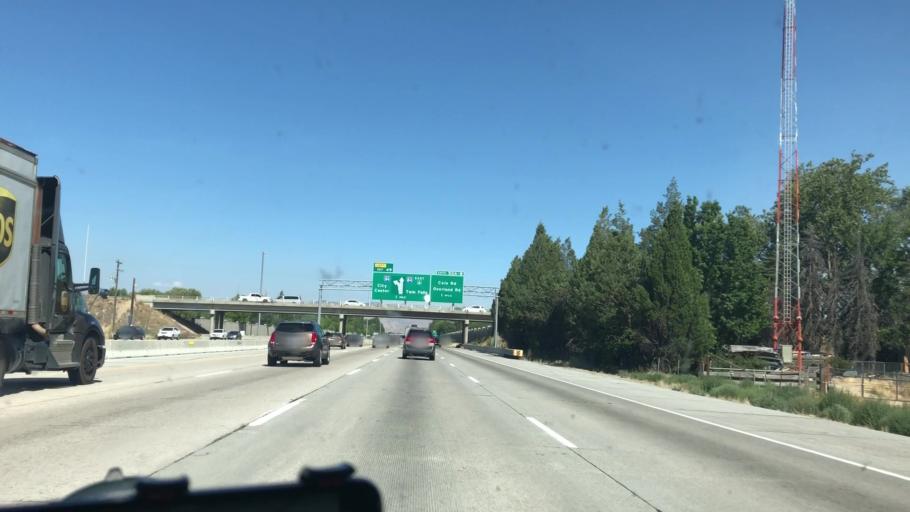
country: US
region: Idaho
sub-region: Ada County
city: Meridian
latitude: 43.5972
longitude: -116.3161
